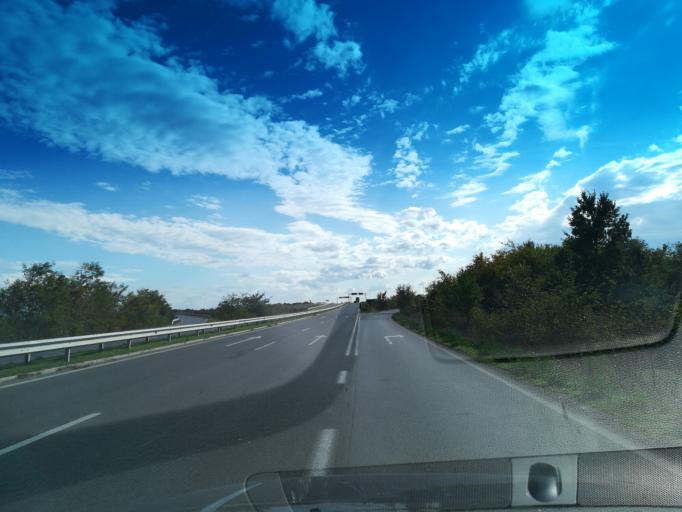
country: BG
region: Stara Zagora
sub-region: Obshtina Stara Zagora
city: Stara Zagora
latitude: 42.3433
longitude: 25.6607
